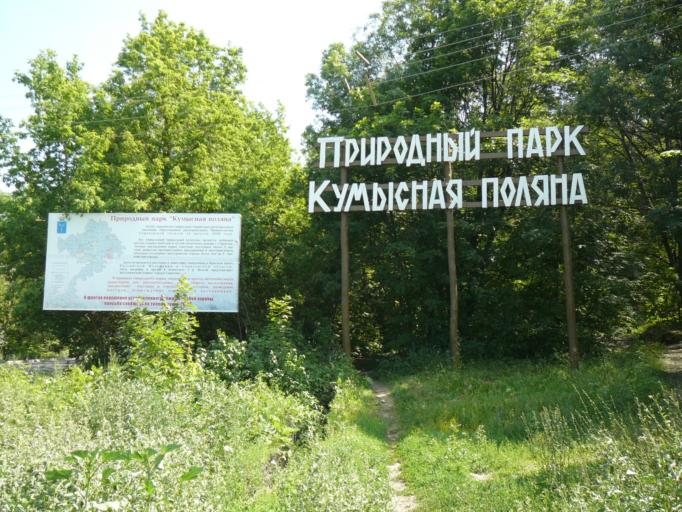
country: RU
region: Saratov
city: Sokolovyy
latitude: 51.5646
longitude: 45.8912
